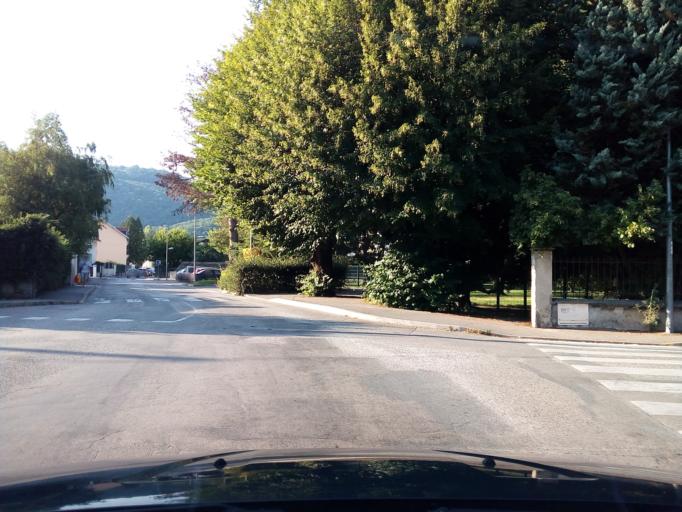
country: FR
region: Rhone-Alpes
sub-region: Departement de l'Isere
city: Vizille
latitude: 45.0789
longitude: 5.7694
